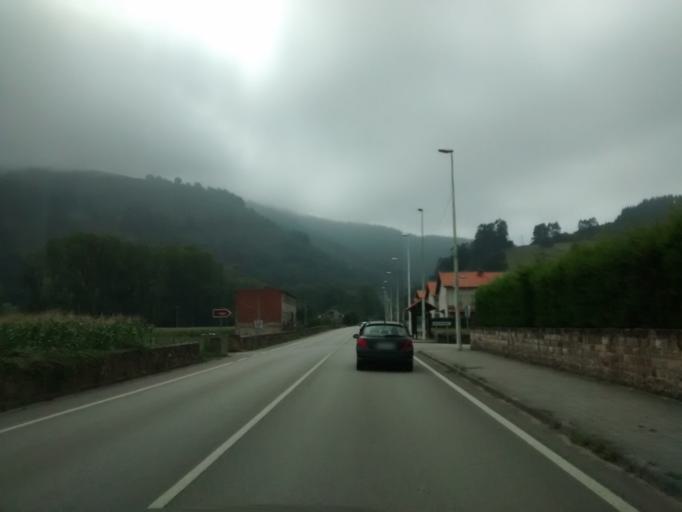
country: ES
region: Cantabria
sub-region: Provincia de Cantabria
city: Cabezon de la Sal
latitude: 43.2894
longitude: -4.2359
